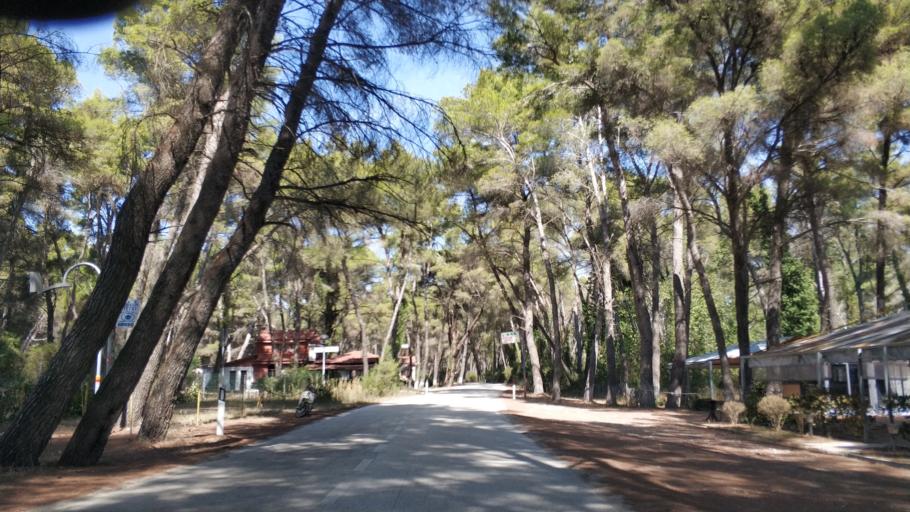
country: AL
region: Fier
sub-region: Rrethi i Lushnjes
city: Divjake
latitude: 40.9743
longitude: 19.4806
